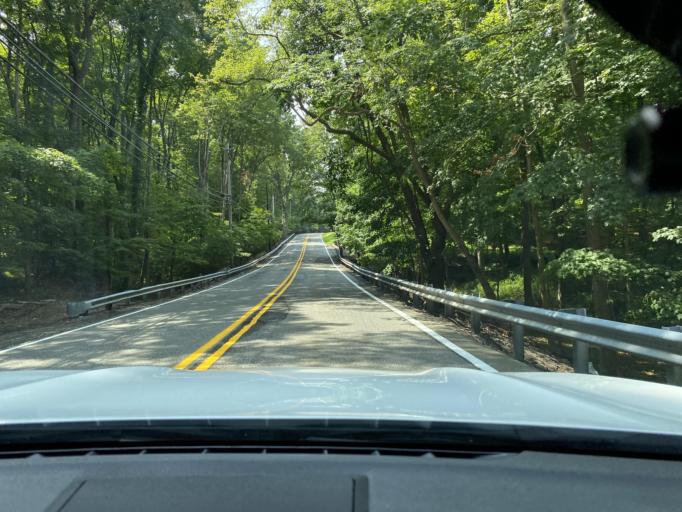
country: US
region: New Jersey
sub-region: Bergen County
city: Franklin Lakes
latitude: 41.0574
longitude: -74.2130
